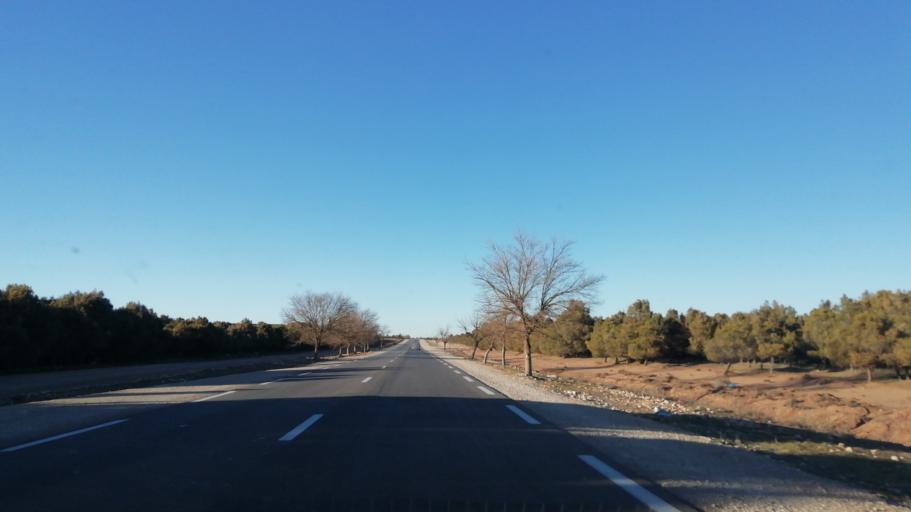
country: DZ
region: Tlemcen
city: Sebdou
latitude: 34.5122
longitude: -1.2839
